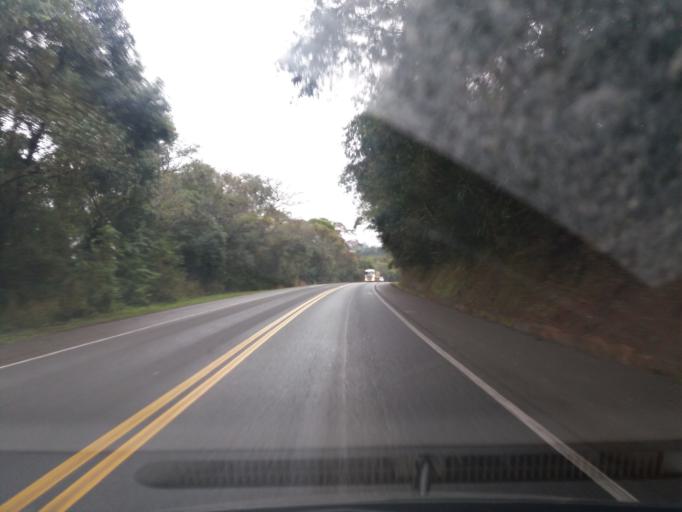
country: BR
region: Parana
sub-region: Ampere
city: Ampere
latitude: -25.9309
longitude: -53.4282
